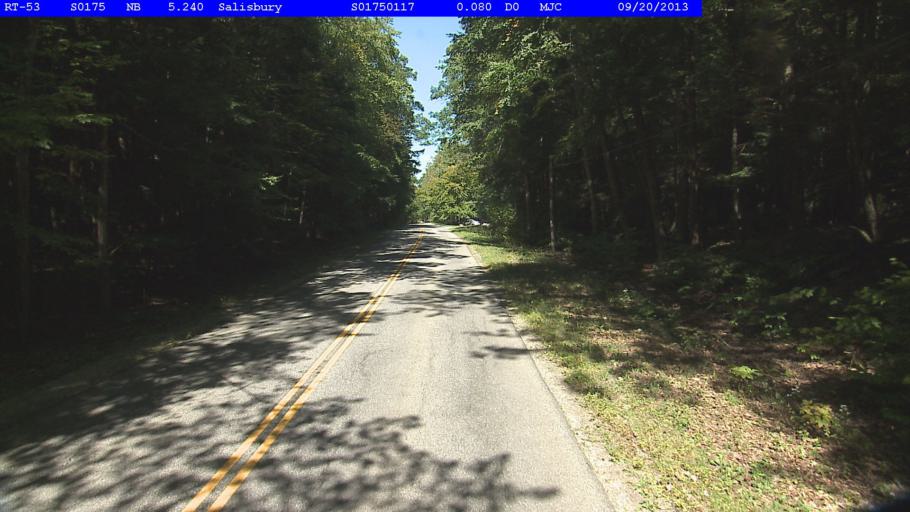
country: US
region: Vermont
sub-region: Rutland County
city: Brandon
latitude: 43.8988
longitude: -73.0640
